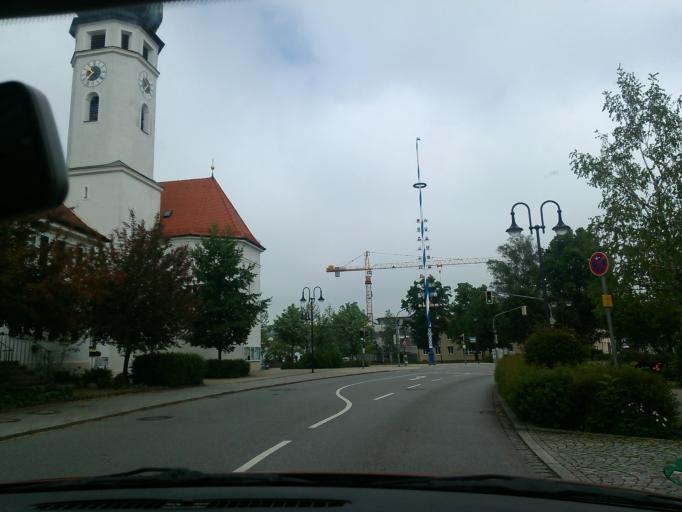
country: DE
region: Bavaria
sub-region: Upper Bavaria
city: Eichenau
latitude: 48.1716
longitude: 11.3223
